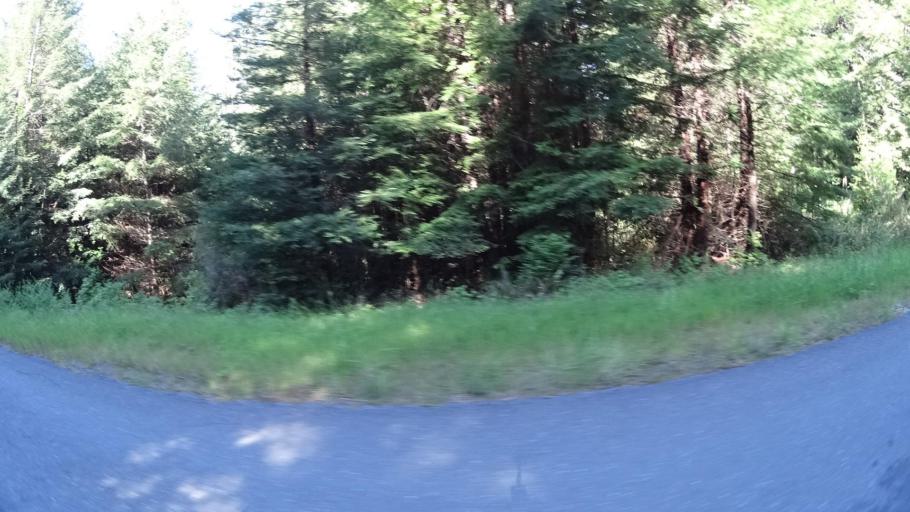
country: US
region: California
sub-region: Humboldt County
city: Rio Dell
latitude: 40.4546
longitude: -124.0263
